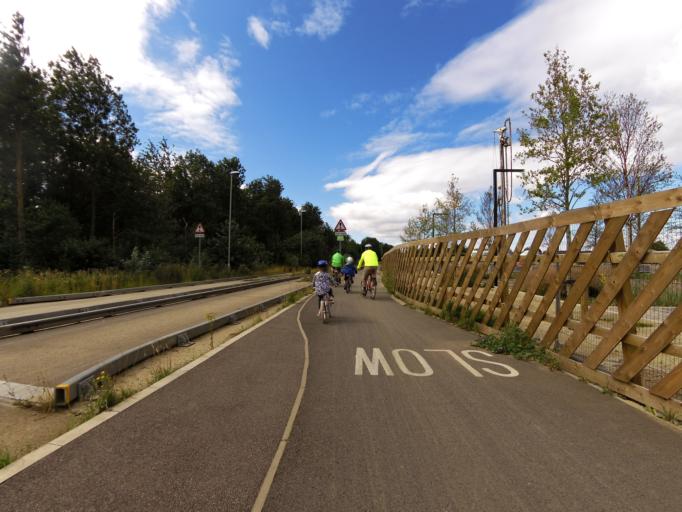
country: GB
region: England
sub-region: Cambridgeshire
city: Cambridge
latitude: 52.1730
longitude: 0.1235
